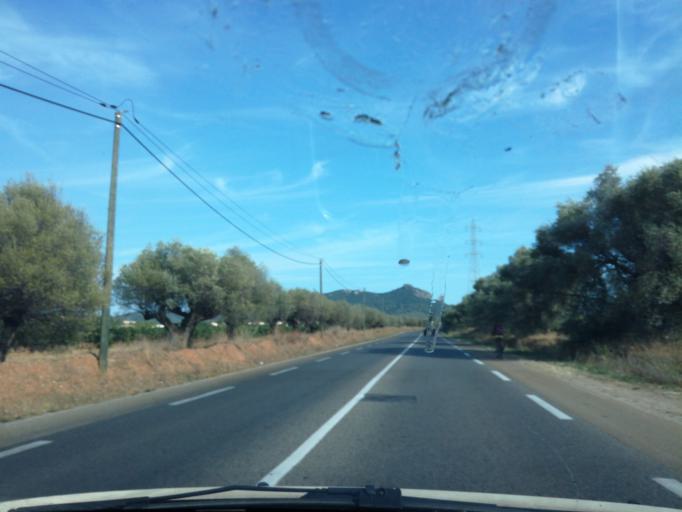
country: FR
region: Provence-Alpes-Cote d'Azur
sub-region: Departement du Var
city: La Crau
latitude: 43.1576
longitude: 6.0661
